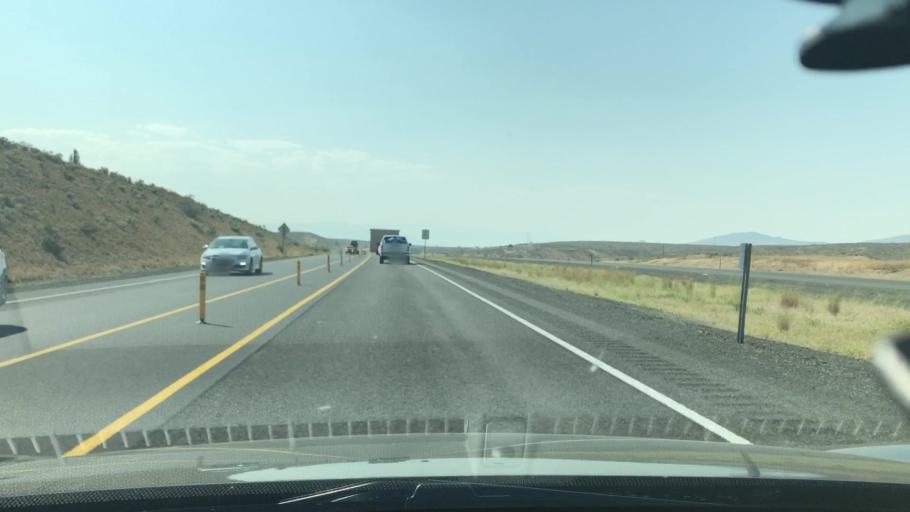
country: US
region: Oregon
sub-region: Baker County
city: Baker City
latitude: 44.6851
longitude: -117.6667
